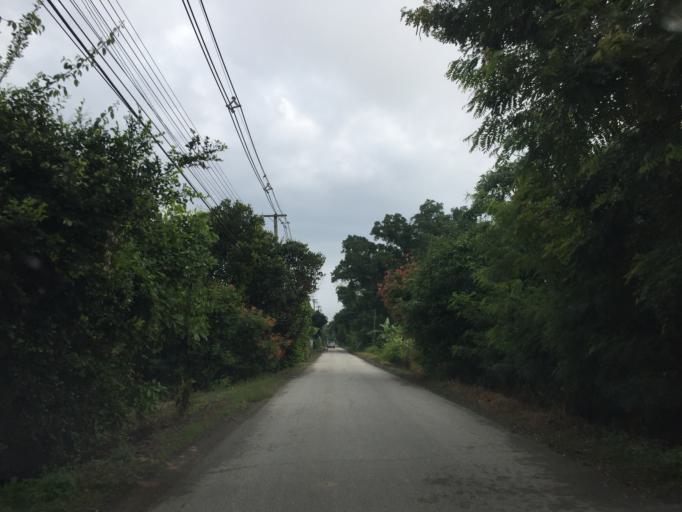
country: TH
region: Lamphun
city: Ban Thi
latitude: 18.6509
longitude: 99.0625
